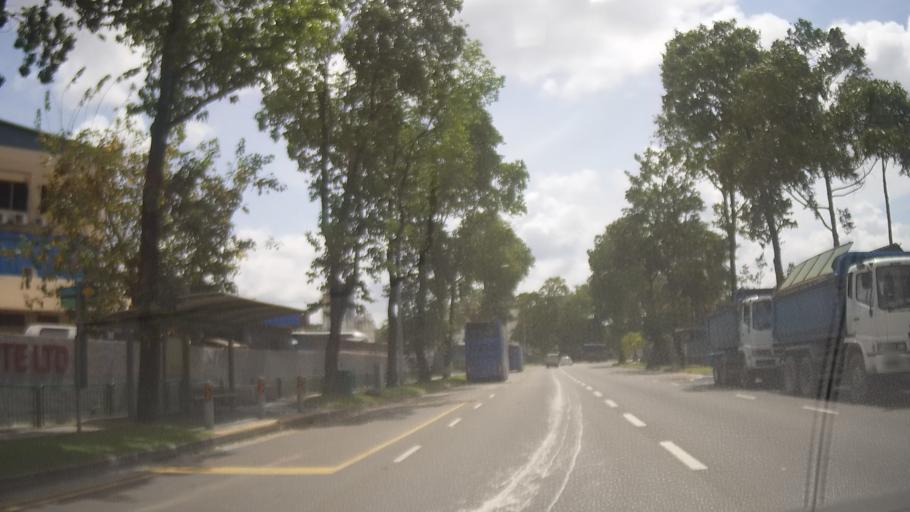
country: MY
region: Johor
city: Johor Bahru
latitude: 1.4261
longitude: 103.7478
